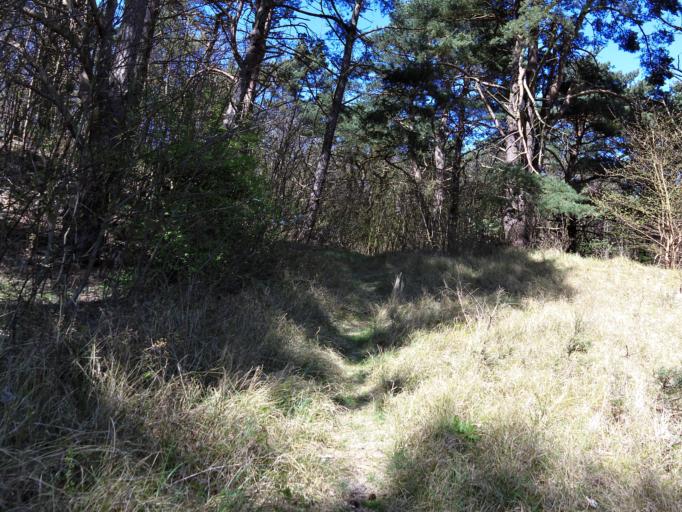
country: DE
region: Mecklenburg-Vorpommern
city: Hiddensee
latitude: 54.5931
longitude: 13.1103
